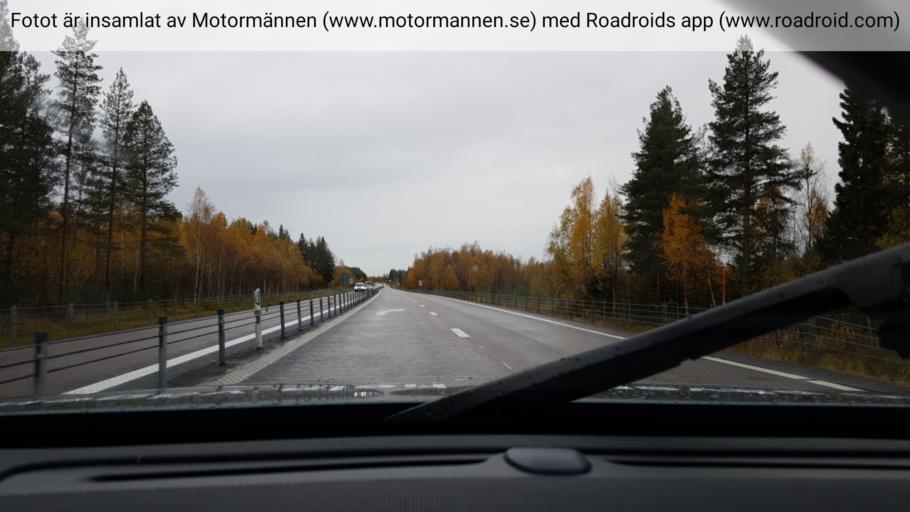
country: SE
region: Norrbotten
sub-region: Pitea Kommun
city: Rosvik
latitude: 65.5236
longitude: 21.7806
